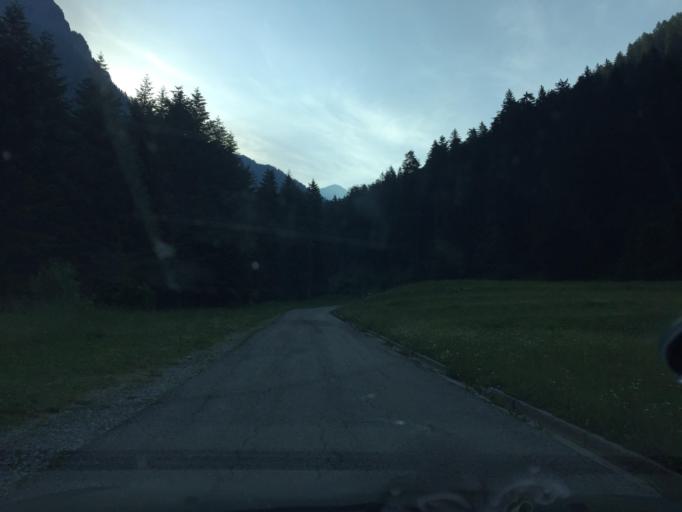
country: IT
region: Friuli Venezia Giulia
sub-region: Provincia di Udine
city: Rigolato
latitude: 46.5912
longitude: 12.8621
